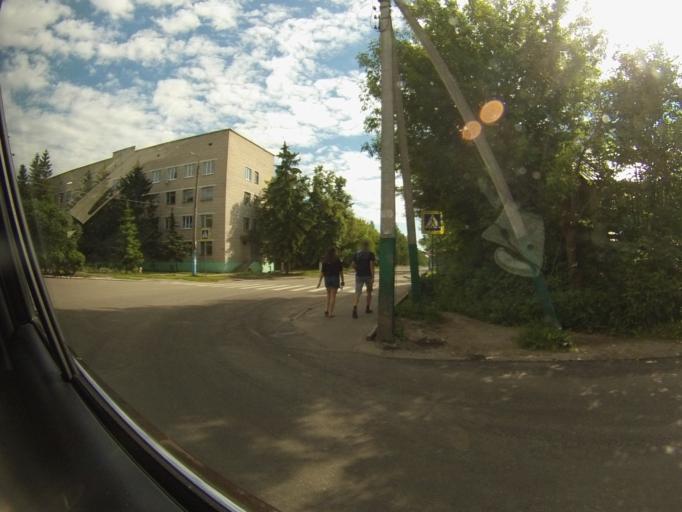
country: RU
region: Orjol
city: Mtsensk
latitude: 53.2874
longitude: 36.5852
